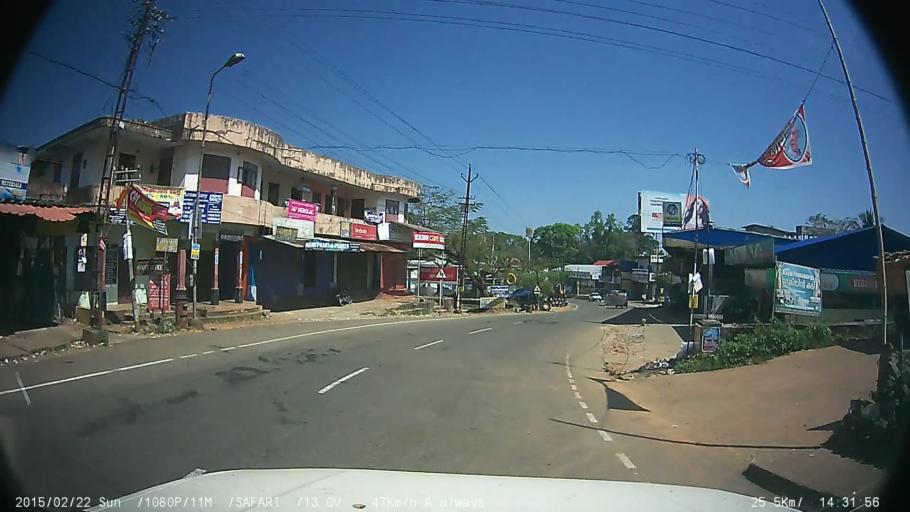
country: IN
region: Kerala
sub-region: Kottayam
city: Erattupetta
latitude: 9.5642
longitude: 76.7579
